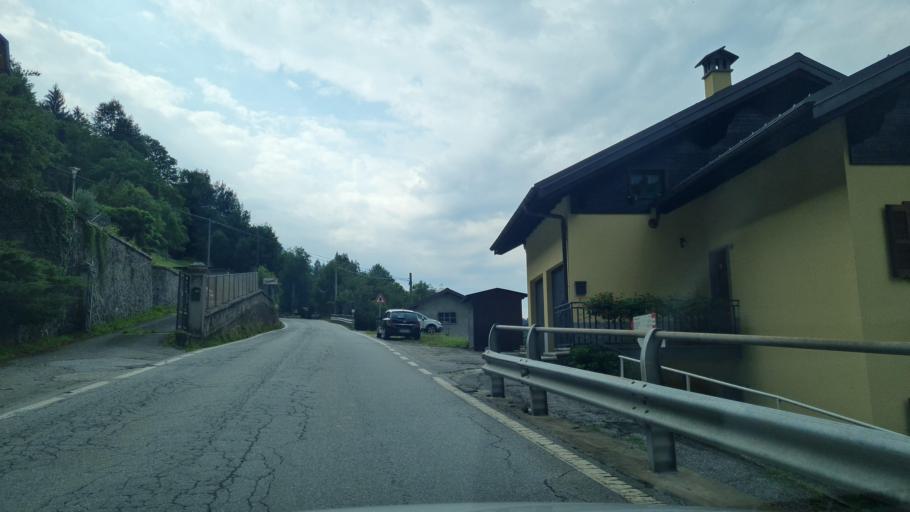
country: IT
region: Piedmont
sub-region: Provincia Verbano-Cusio-Ossola
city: Baceno
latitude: 46.2608
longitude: 8.3208
